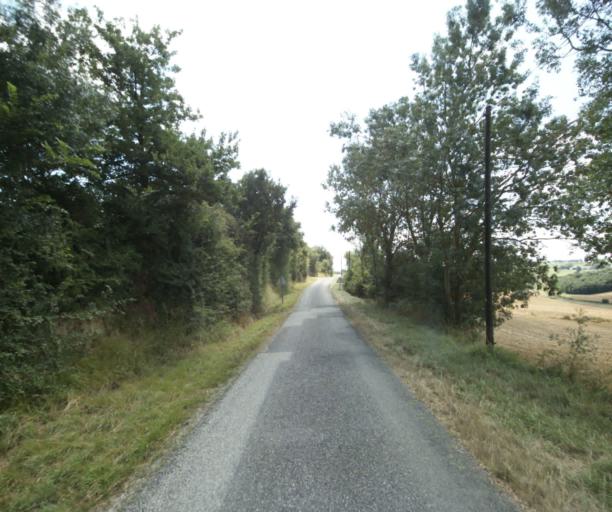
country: FR
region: Midi-Pyrenees
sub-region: Departement de la Haute-Garonne
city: Auriac-sur-Vendinelle
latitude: 43.4774
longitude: 1.8193
